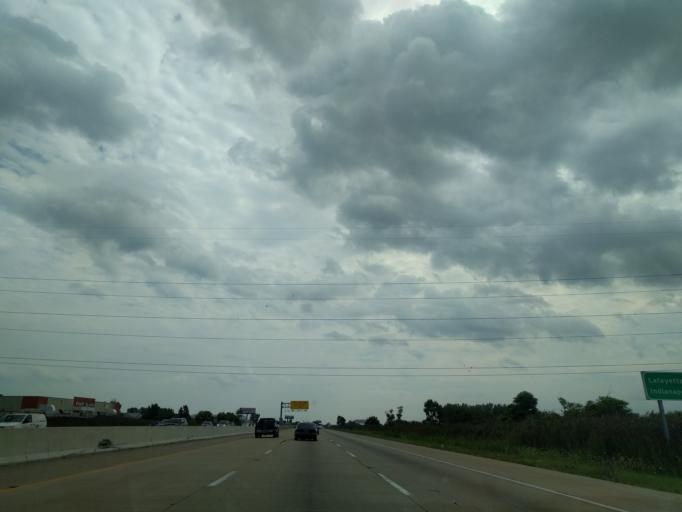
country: US
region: Indiana
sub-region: Lake County
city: Merrillville
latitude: 41.4609
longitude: -87.3228
